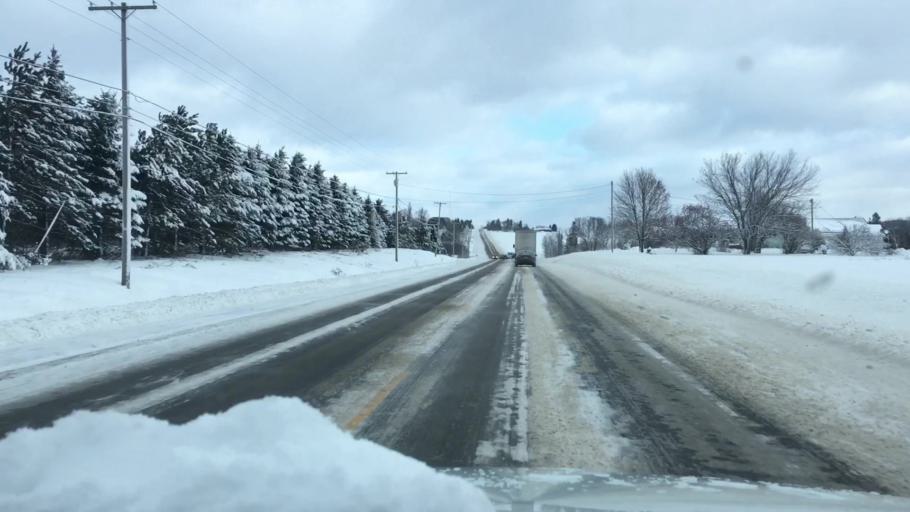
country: US
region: Maine
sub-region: Aroostook County
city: Presque Isle
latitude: 46.7440
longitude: -67.9957
